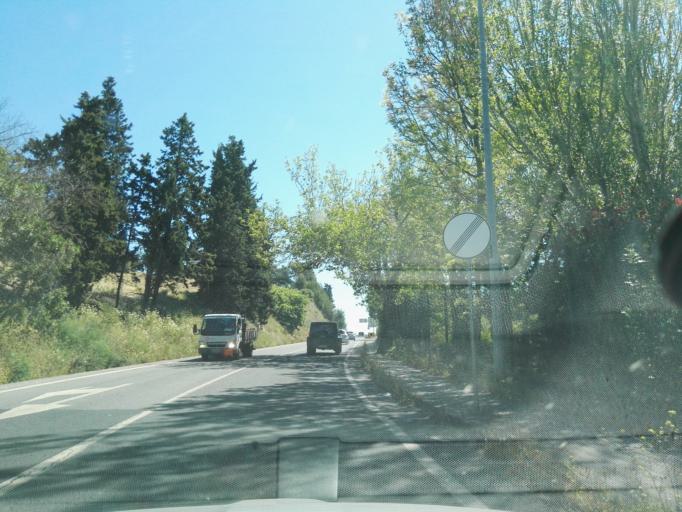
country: PT
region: Lisbon
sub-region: Loures
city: Sacavem
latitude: 38.7991
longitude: -9.1034
